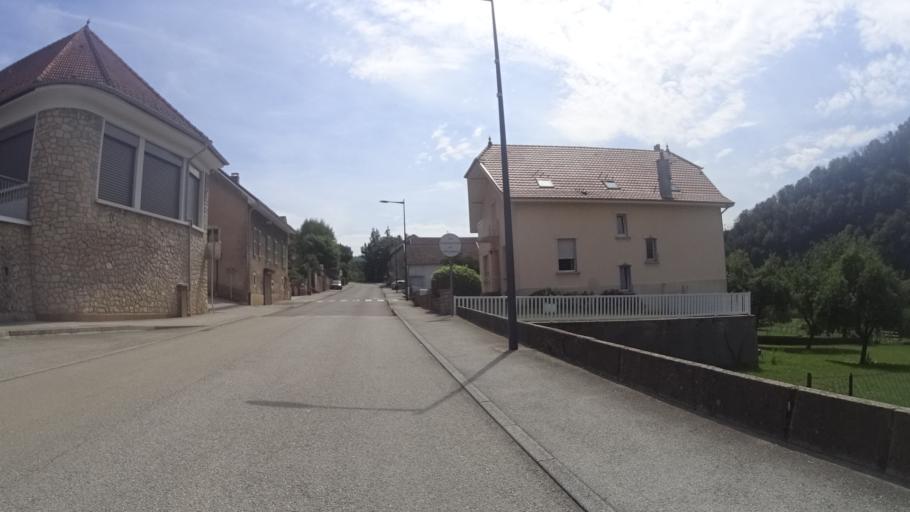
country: FR
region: Franche-Comte
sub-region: Departement du Doubs
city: Clerval
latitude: 47.3913
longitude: 6.4991
